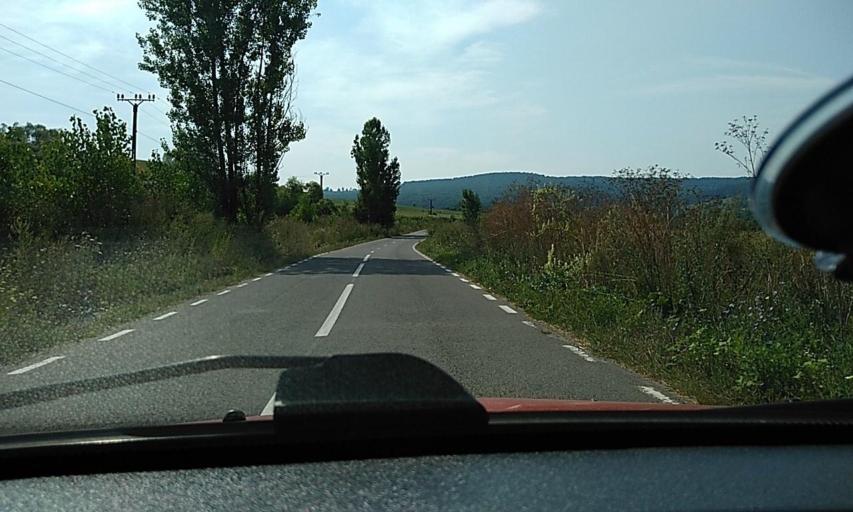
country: RO
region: Brasov
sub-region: Oras Rupea
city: Fiser
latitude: 46.0200
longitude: 25.1502
